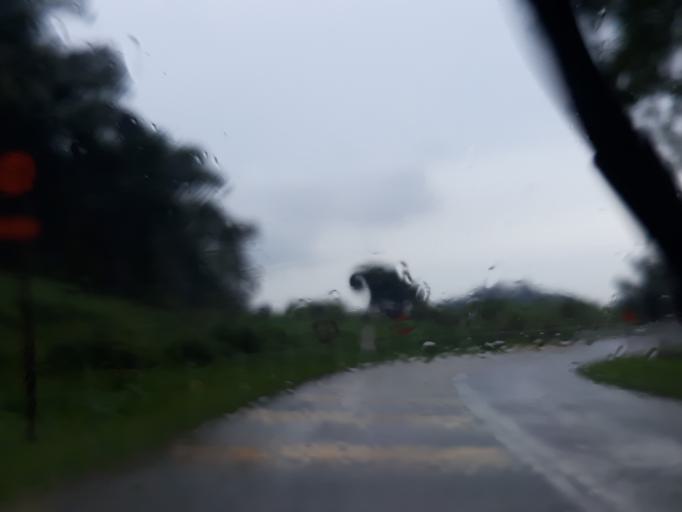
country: MY
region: Kedah
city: Kulim
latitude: 5.3462
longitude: 100.5859
